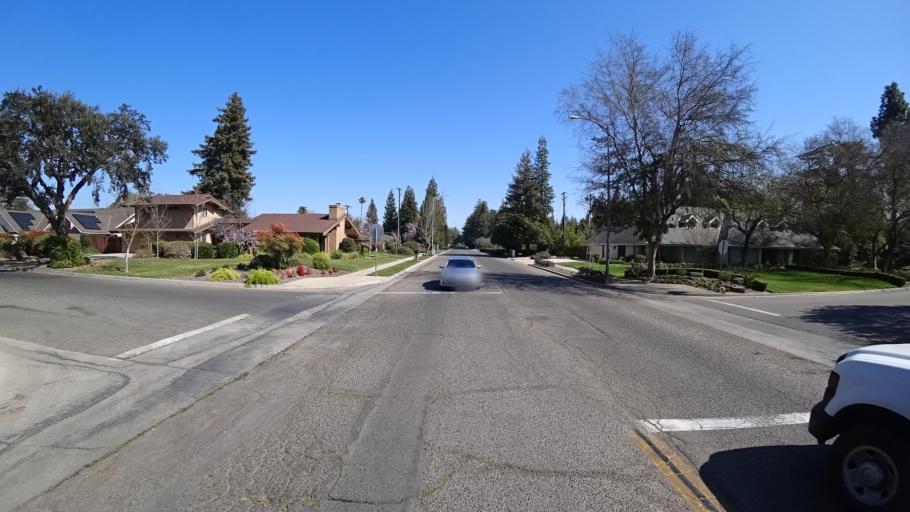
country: US
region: California
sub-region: Fresno County
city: Fresno
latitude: 36.8300
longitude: -119.8407
